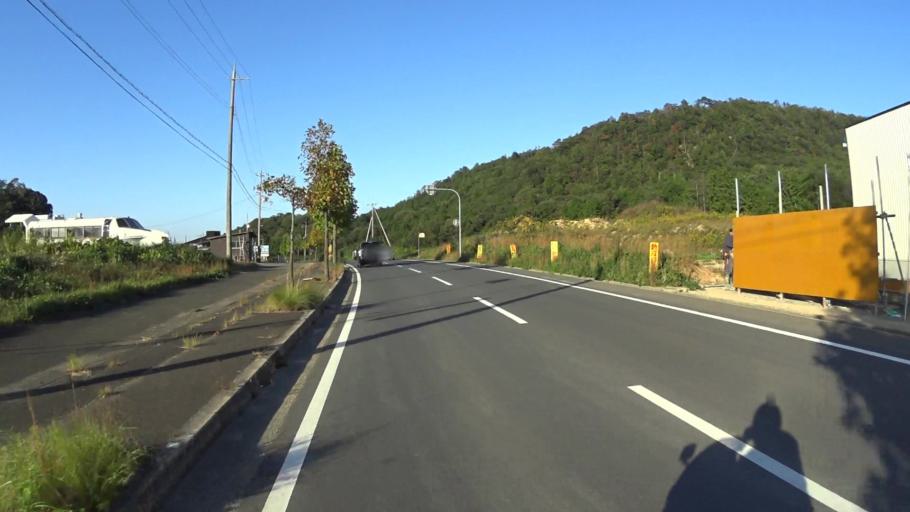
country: JP
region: Hyogo
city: Toyooka
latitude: 35.6216
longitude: 134.9278
